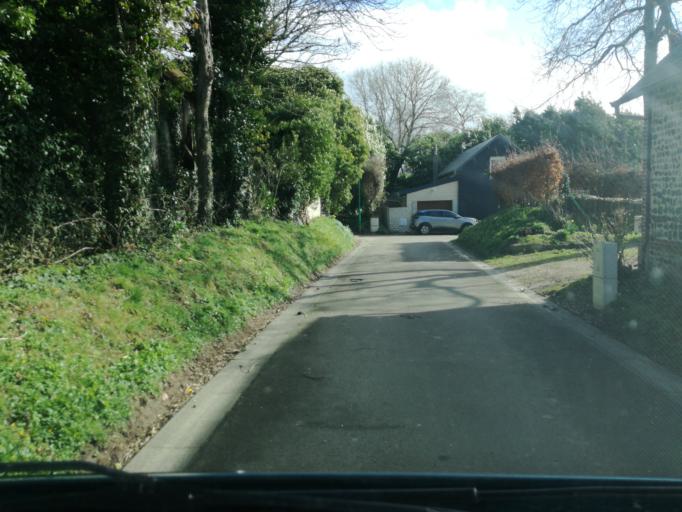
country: FR
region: Haute-Normandie
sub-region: Departement de la Seine-Maritime
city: Saint-Leonard
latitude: 49.7381
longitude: 0.3392
